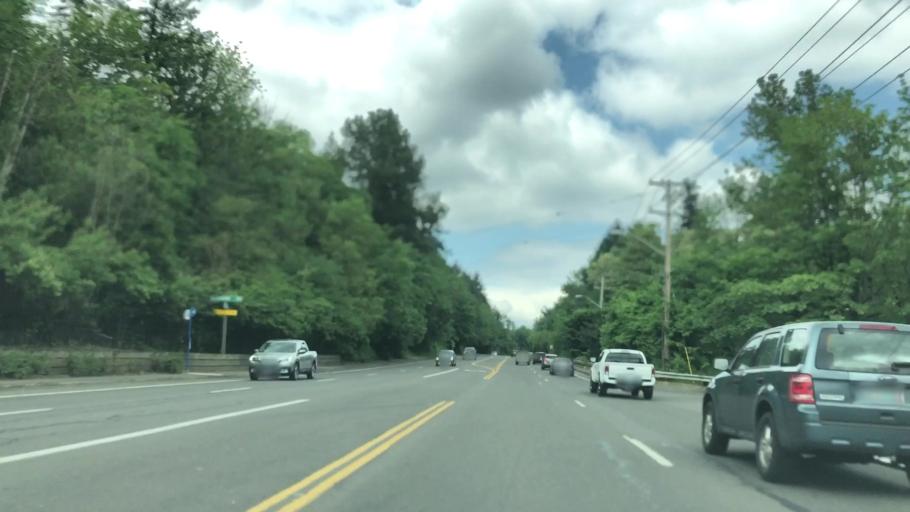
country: US
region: Oregon
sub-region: Clackamas County
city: Lake Oswego
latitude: 45.4210
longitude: -122.7109
